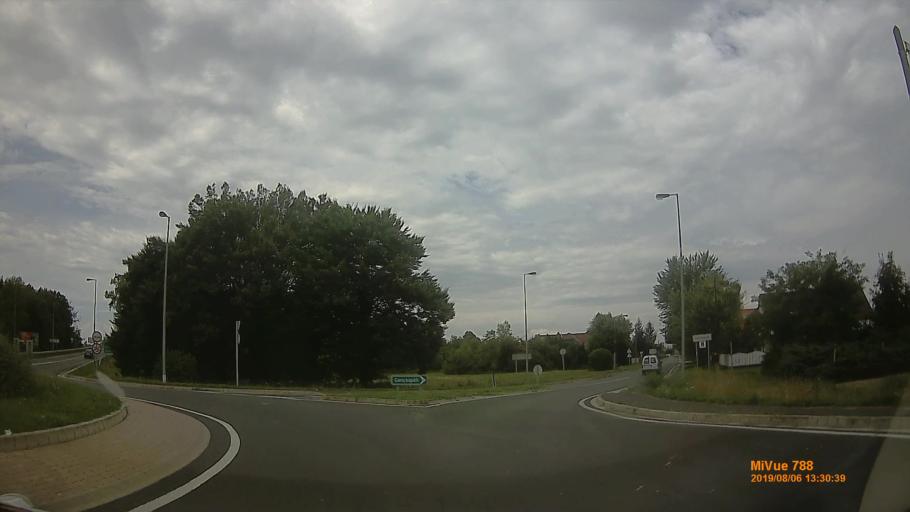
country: HU
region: Vas
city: Gencsapati
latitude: 47.2646
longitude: 16.6038
